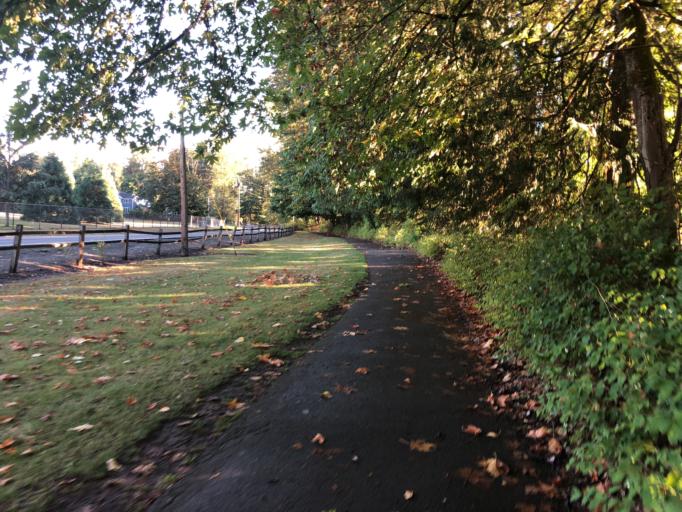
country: US
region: Washington
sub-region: King County
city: Auburn
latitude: 47.3314
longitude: -122.2117
